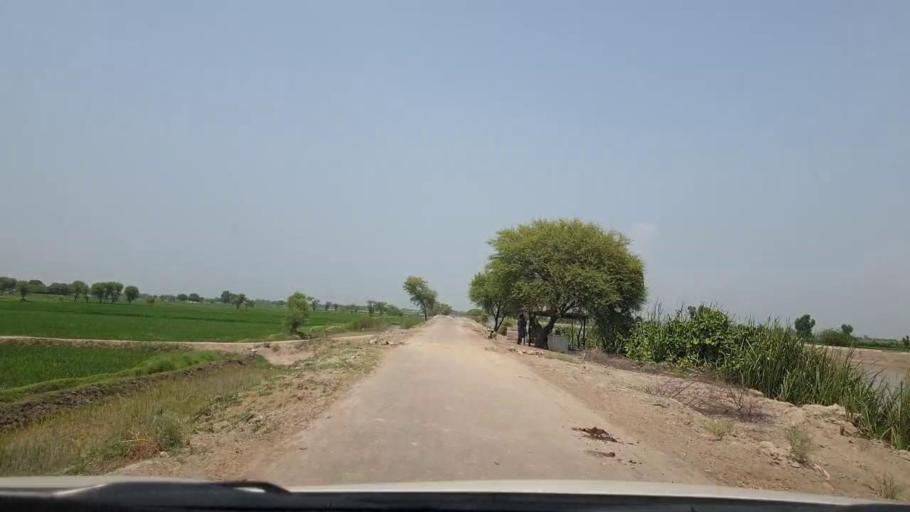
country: PK
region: Sindh
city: Dokri
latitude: 27.3386
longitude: 68.1106
